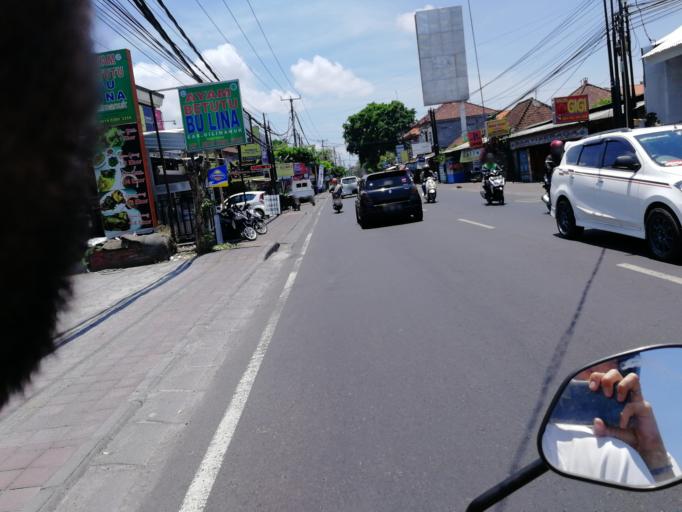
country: ID
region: Bali
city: Karyadharma
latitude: -8.6857
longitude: 115.1940
